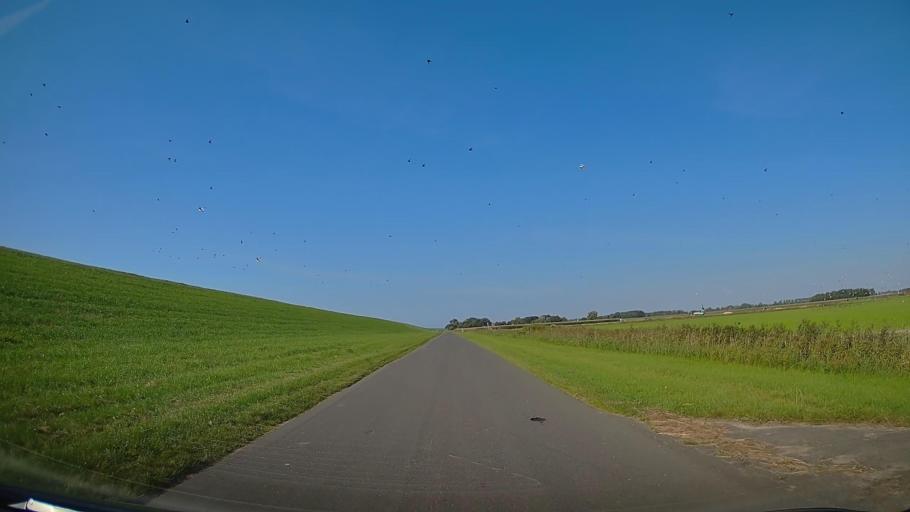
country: DE
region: Lower Saxony
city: Misselwarden
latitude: 53.6637
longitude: 8.4884
